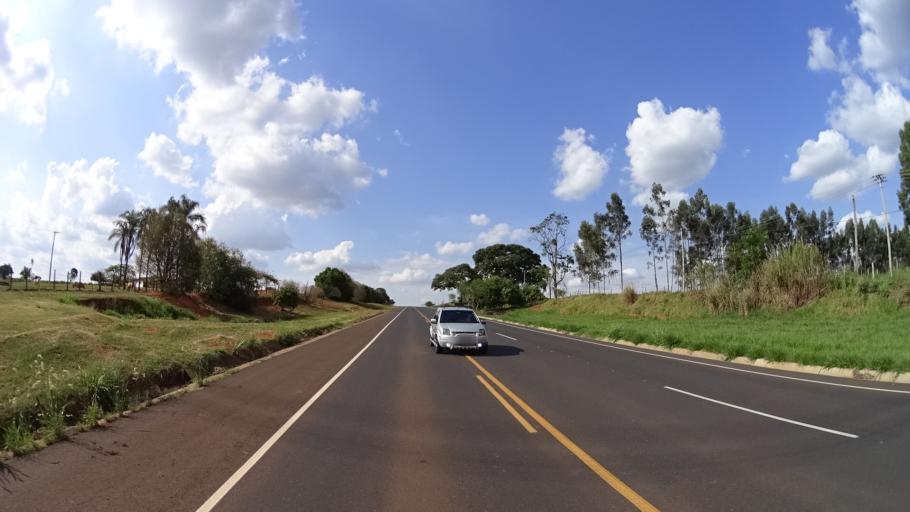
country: BR
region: Sao Paulo
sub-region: Urupes
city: Urupes
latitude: -21.0561
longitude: -49.2486
